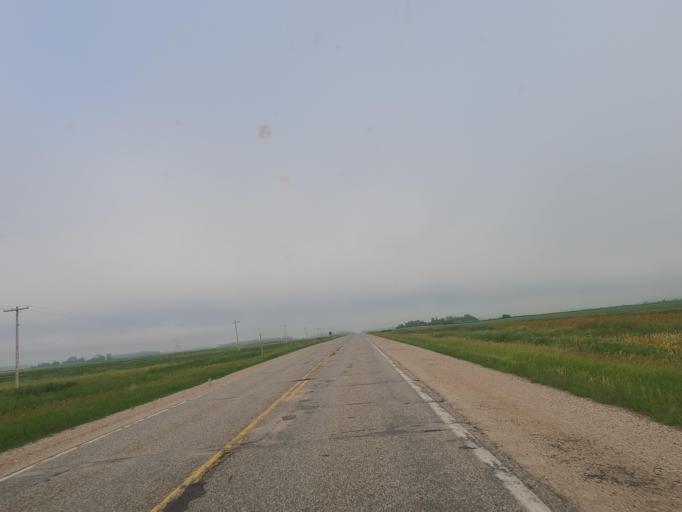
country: CA
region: Manitoba
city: Carman
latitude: 49.6652
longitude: -98.2160
